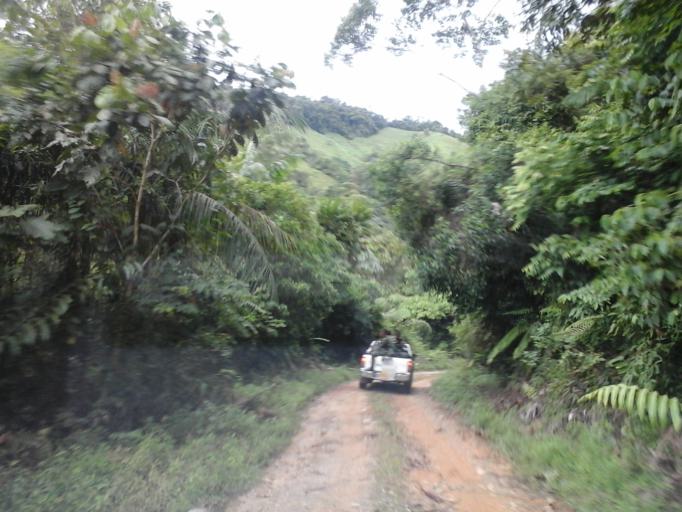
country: CO
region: Antioquia
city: San Roque
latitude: 6.4993
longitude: -74.9762
